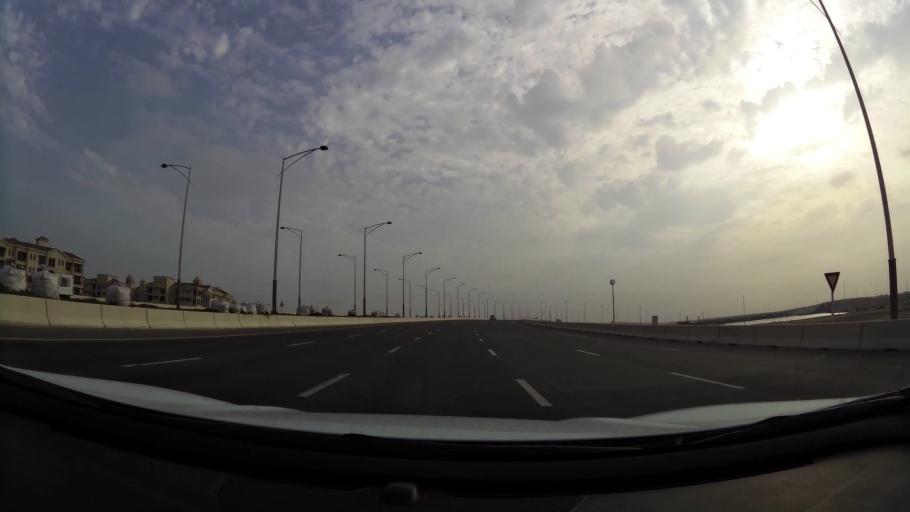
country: AE
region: Abu Dhabi
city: Abu Dhabi
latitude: 24.5481
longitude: 54.4531
